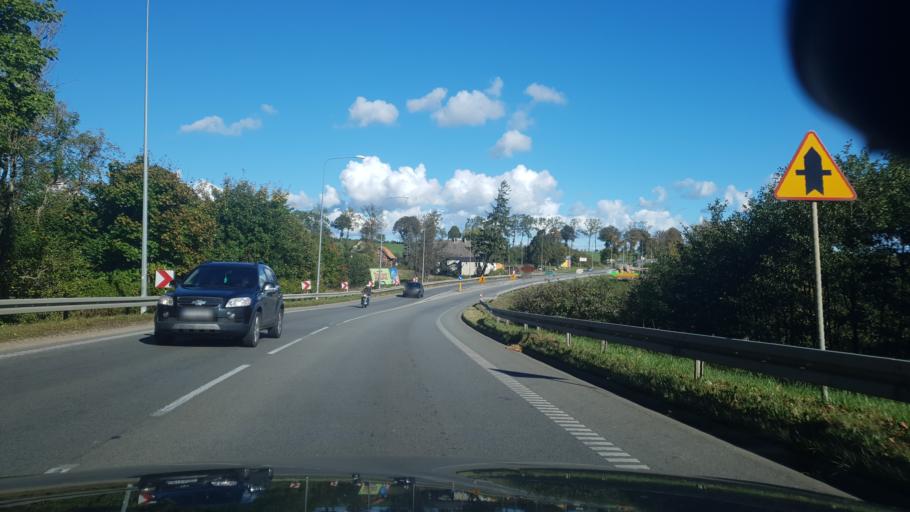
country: PL
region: Pomeranian Voivodeship
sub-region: Powiat wejherowski
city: Rekowo Dolne
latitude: 54.6606
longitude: 18.3619
